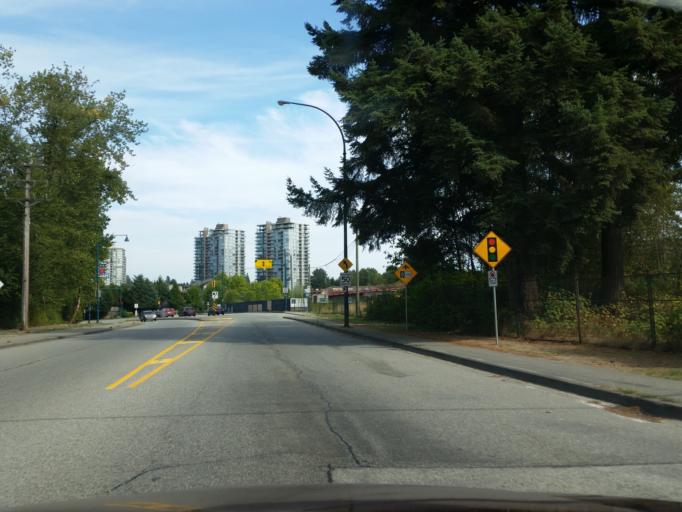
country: CA
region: British Columbia
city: Port Moody
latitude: 49.2788
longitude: -122.8414
